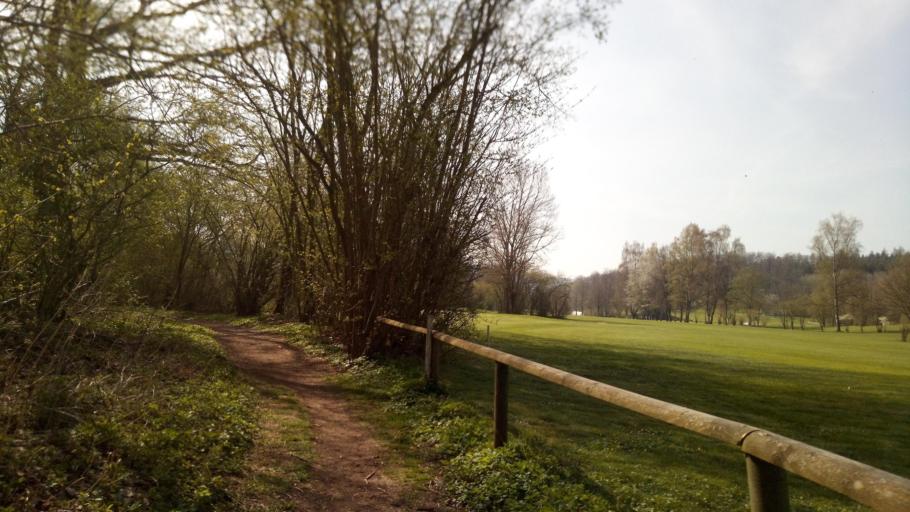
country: DE
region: Baden-Wuerttemberg
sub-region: Regierungsbezirk Stuttgart
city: Donzdorf
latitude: 48.6988
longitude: 9.7993
